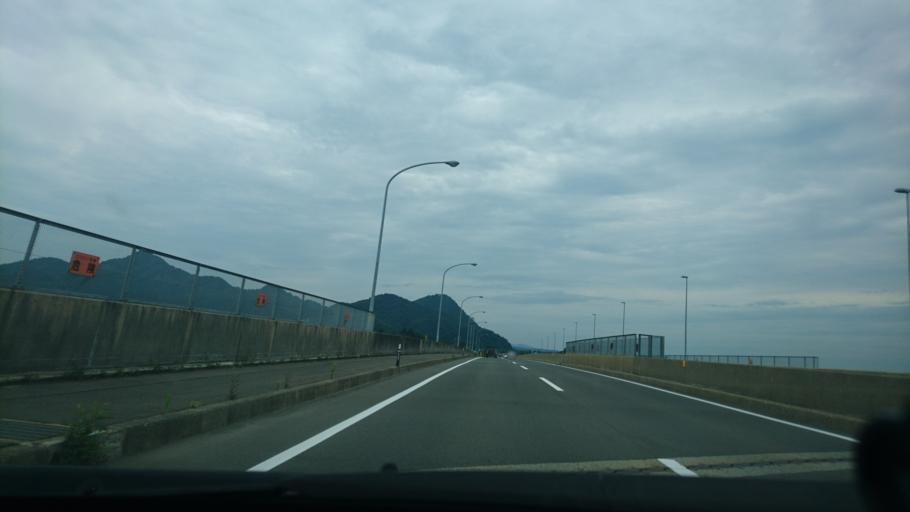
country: JP
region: Akita
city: Omagari
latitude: 39.4763
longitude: 140.4688
